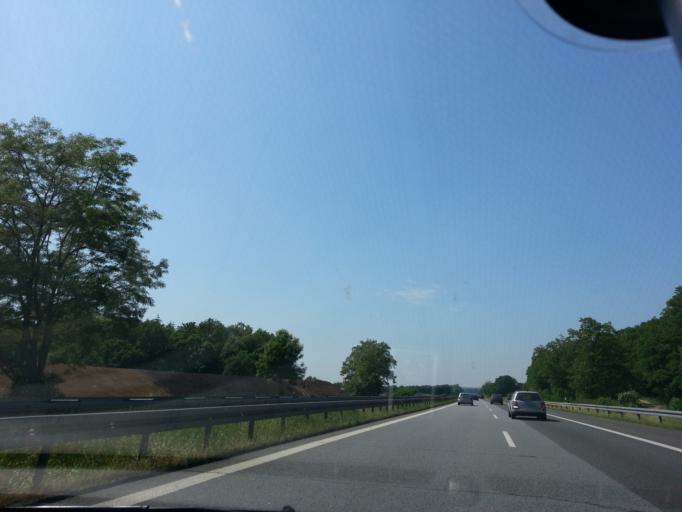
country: DE
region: Brandenburg
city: Triglitz
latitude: 53.2670
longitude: 12.1324
